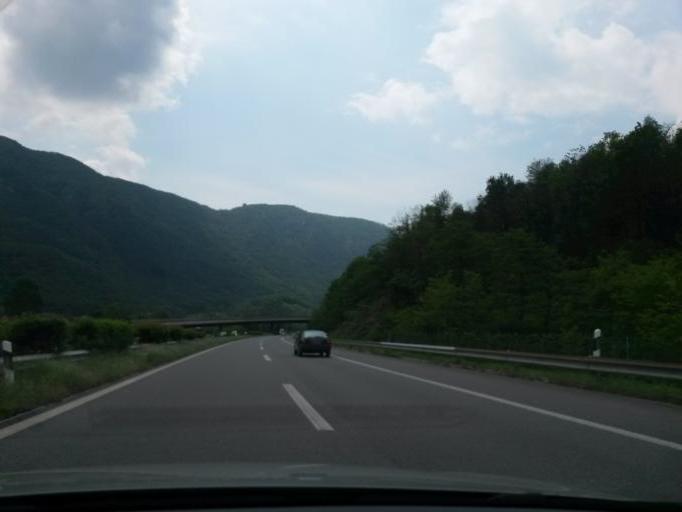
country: CH
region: Ticino
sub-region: Bellinzona District
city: Cadenazzo
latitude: 46.1102
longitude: 8.9304
